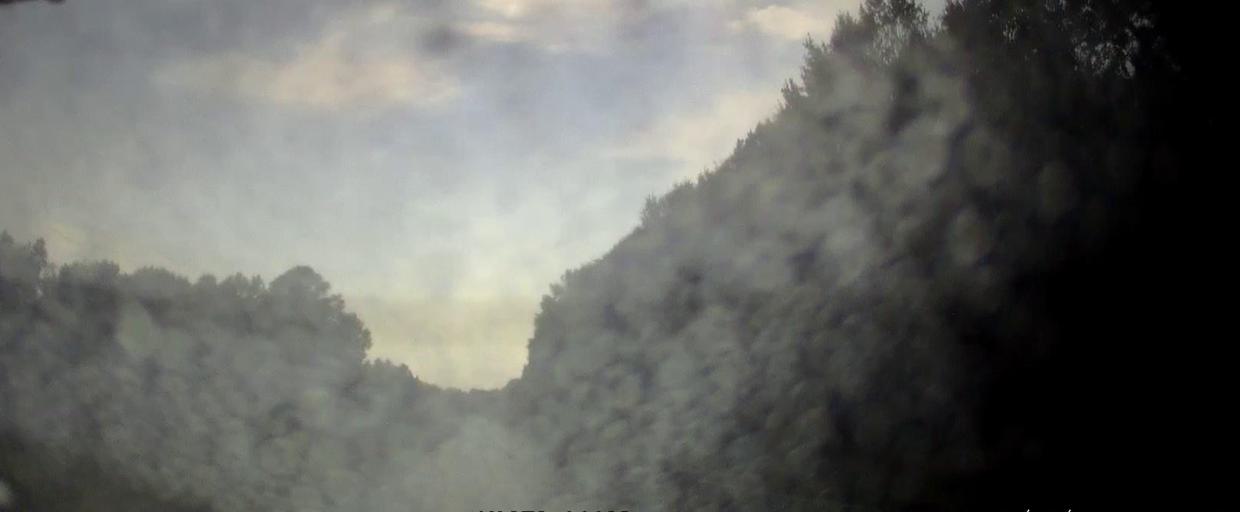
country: US
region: Georgia
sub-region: Dodge County
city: Chester
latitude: 32.5531
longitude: -83.1410
